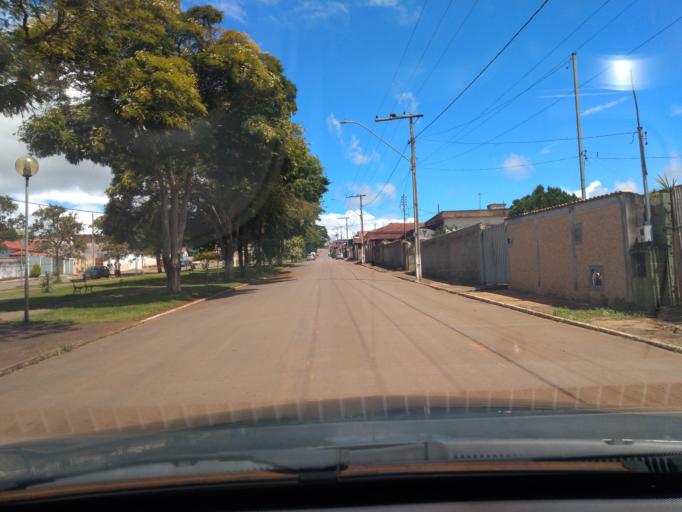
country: BR
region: Minas Gerais
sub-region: Tres Coracoes
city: Tres Coracoes
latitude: -21.5869
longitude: -45.0705
